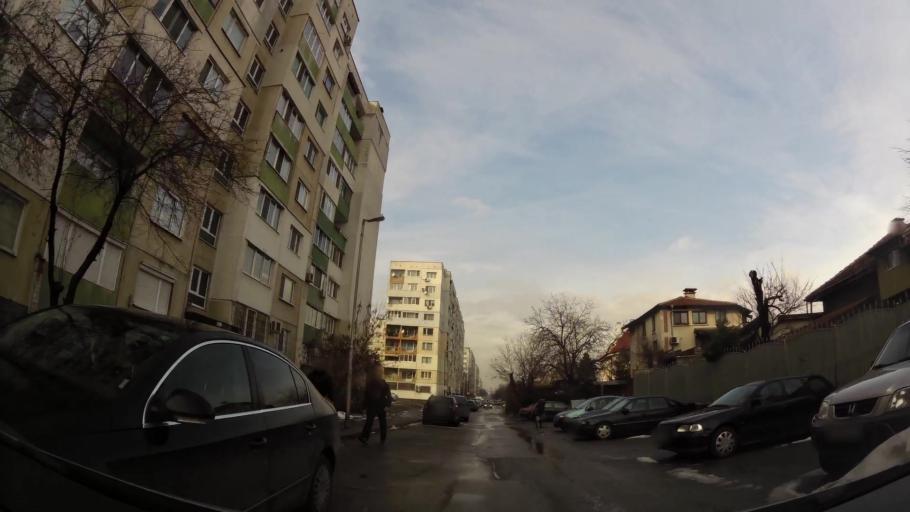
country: BG
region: Sofia-Capital
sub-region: Stolichna Obshtina
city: Sofia
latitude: 42.7193
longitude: 23.2707
